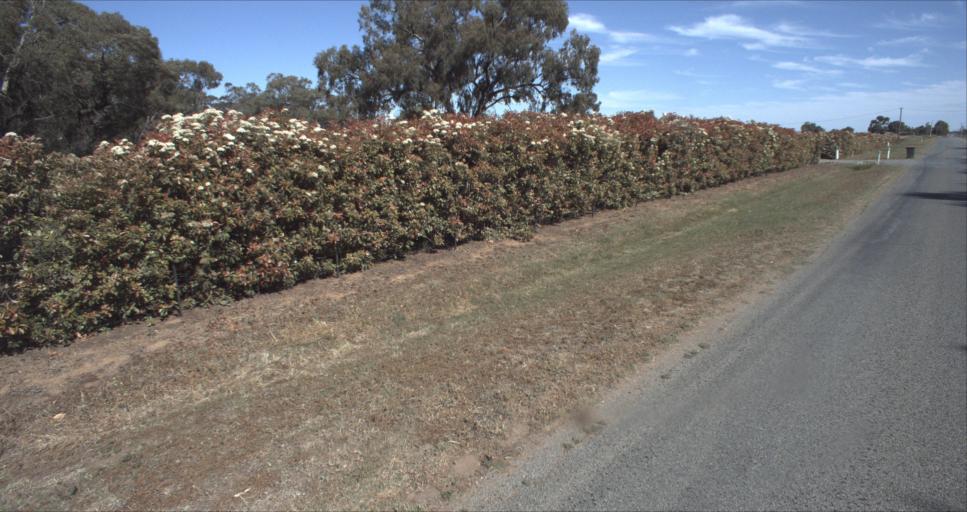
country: AU
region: New South Wales
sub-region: Leeton
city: Leeton
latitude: -34.5586
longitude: 146.3840
